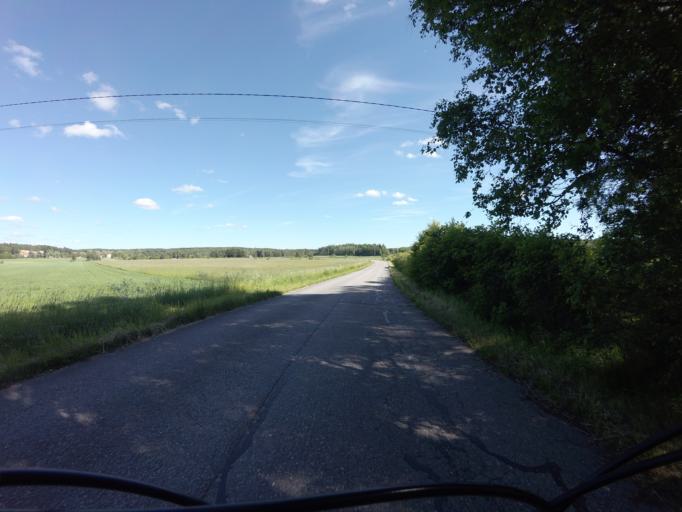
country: FI
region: Varsinais-Suomi
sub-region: Turku
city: Vahto
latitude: 60.5378
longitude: 22.3336
